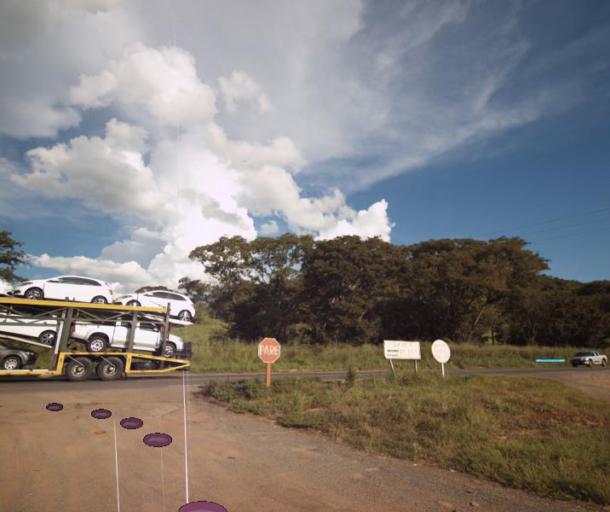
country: BR
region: Goias
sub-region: Rialma
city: Rialma
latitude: -15.2757
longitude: -49.5519
